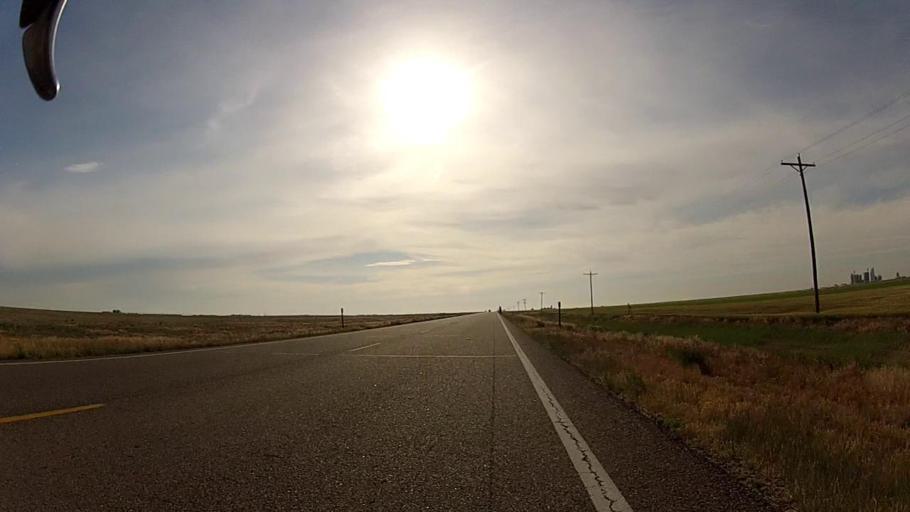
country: US
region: Kansas
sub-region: Grant County
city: Ulysses
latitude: 37.5766
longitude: -101.4707
